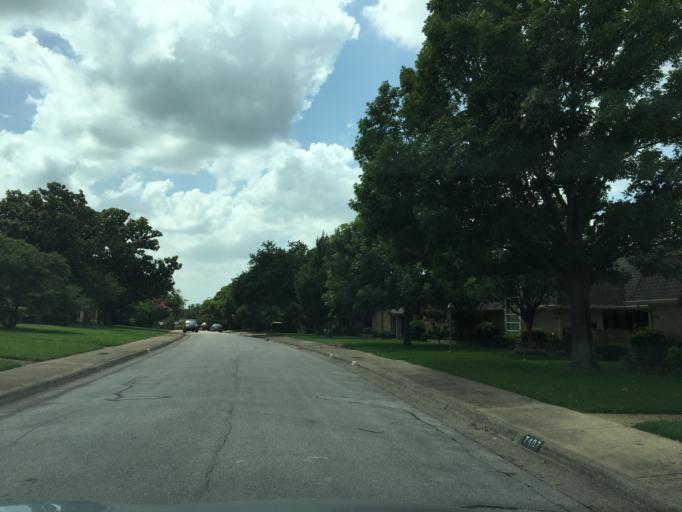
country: US
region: Texas
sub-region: Dallas County
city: University Park
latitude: 32.8886
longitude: -96.7780
